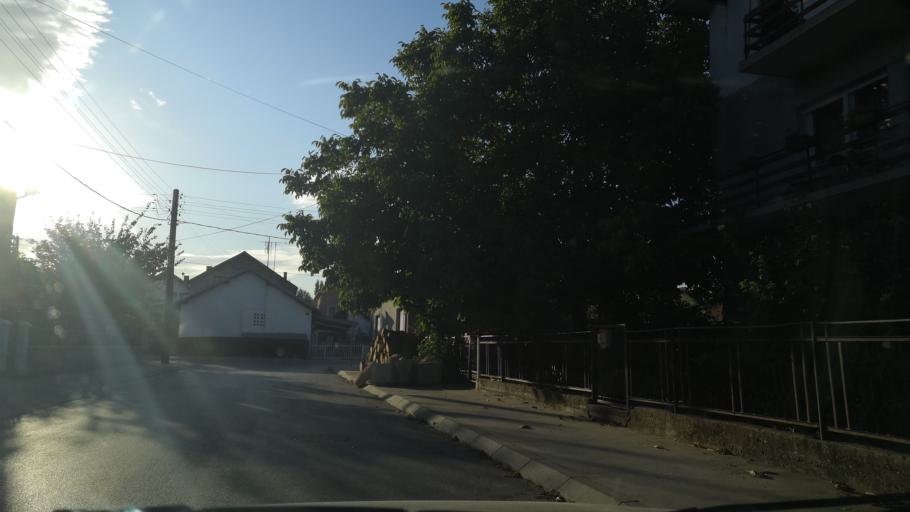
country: RS
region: Central Serbia
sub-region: Borski Okrug
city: Negotin
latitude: 44.2250
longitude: 22.5232
